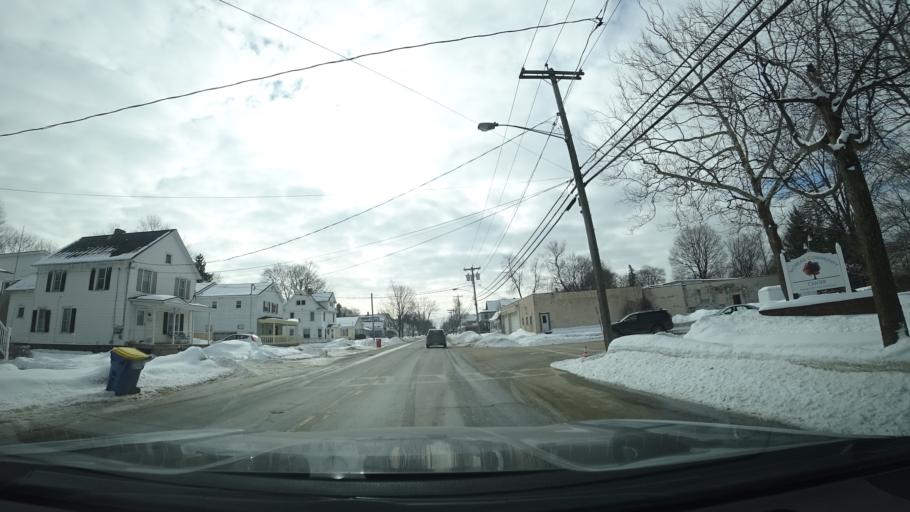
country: US
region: New York
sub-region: Saratoga County
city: South Glens Falls
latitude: 43.2974
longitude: -73.6336
